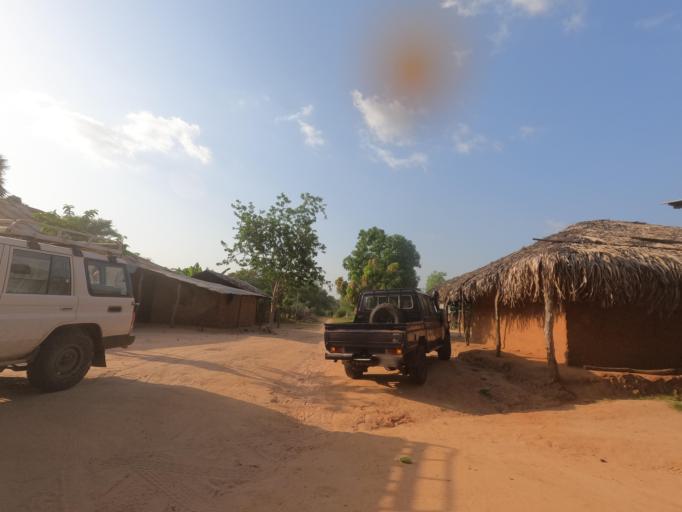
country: GW
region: Oio
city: Bissora
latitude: 12.3385
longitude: -15.6789
